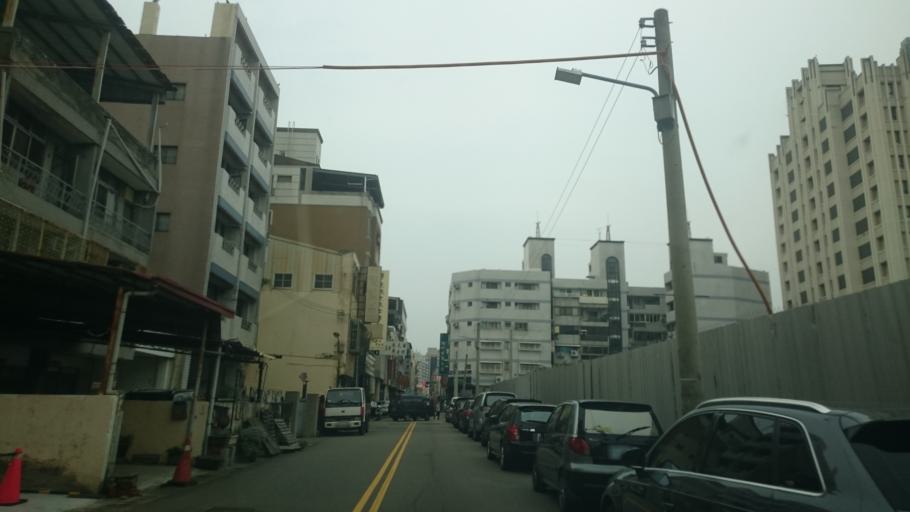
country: TW
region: Taiwan
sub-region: Taichung City
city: Taichung
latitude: 24.1759
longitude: 120.6382
